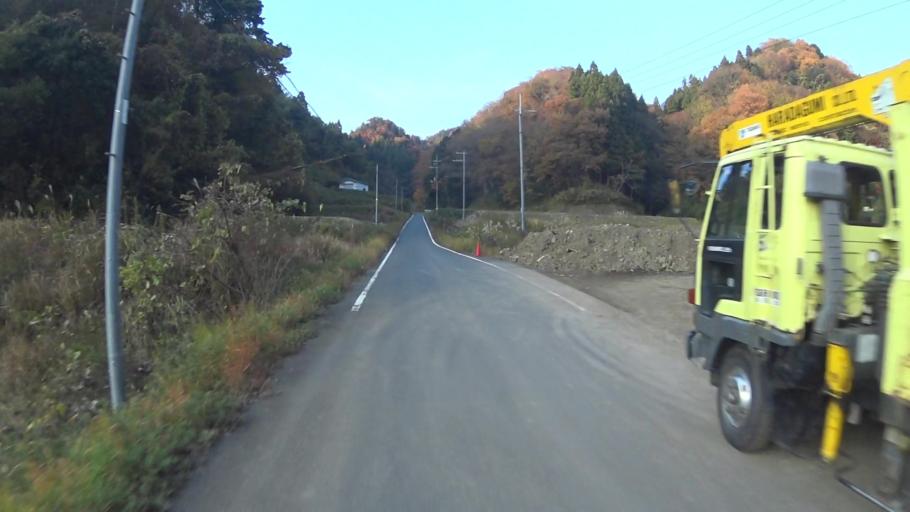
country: JP
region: Kyoto
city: Maizuru
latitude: 35.4894
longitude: 135.4660
